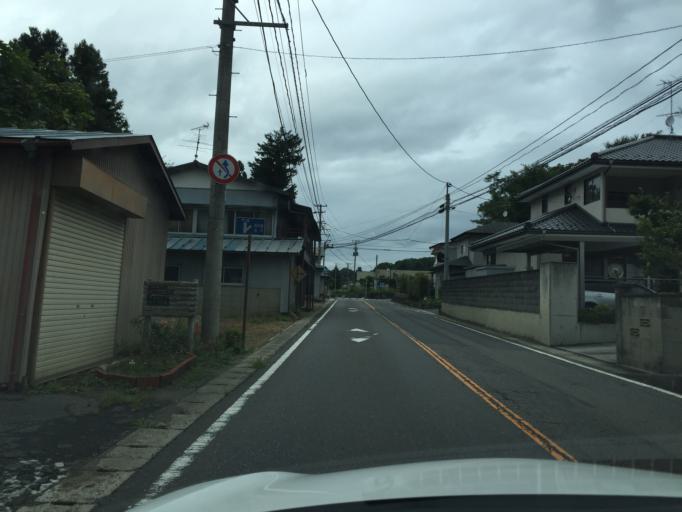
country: JP
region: Fukushima
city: Funehikimachi-funehiki
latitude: 37.4589
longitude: 140.5756
